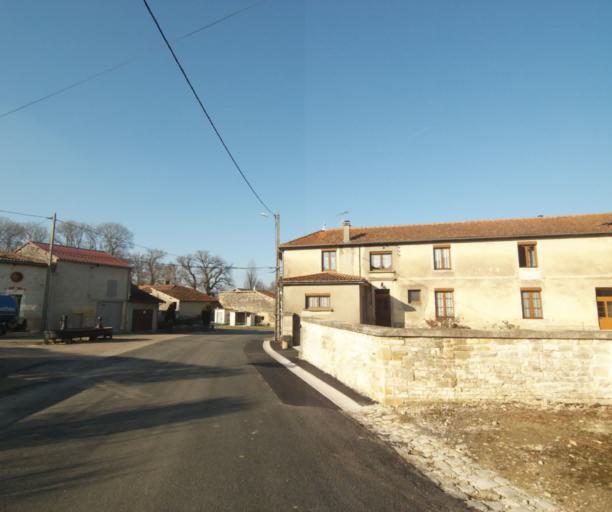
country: FR
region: Champagne-Ardenne
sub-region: Departement de la Haute-Marne
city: Chevillon
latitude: 48.4924
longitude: 5.0681
